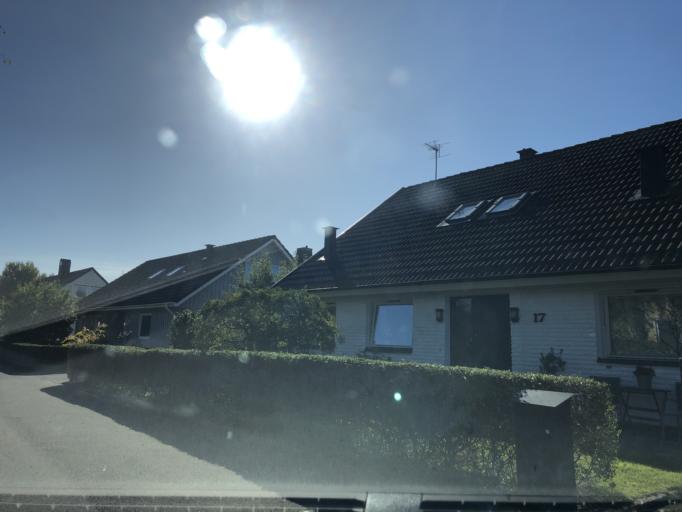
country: SE
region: Vaestra Goetaland
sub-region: Goteborg
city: Majorna
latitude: 57.6612
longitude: 11.8735
